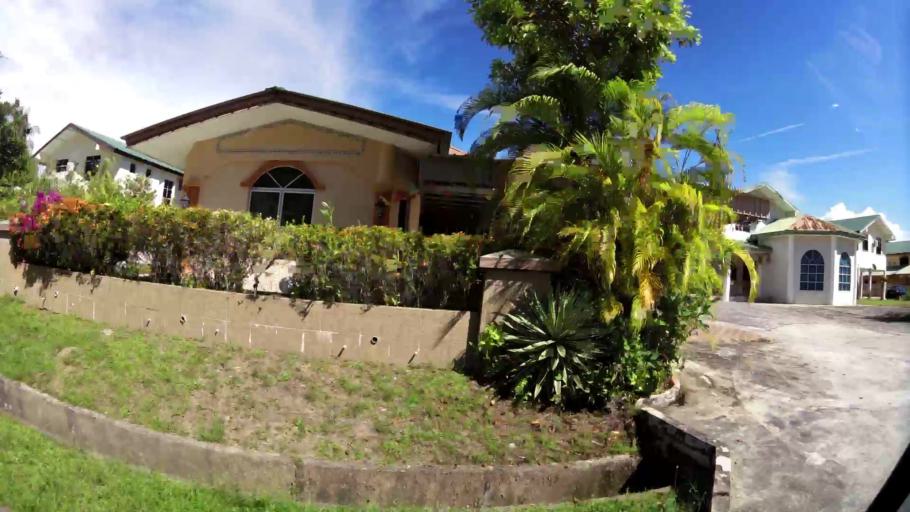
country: BN
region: Brunei and Muara
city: Bandar Seri Begawan
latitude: 5.0037
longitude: 115.0460
